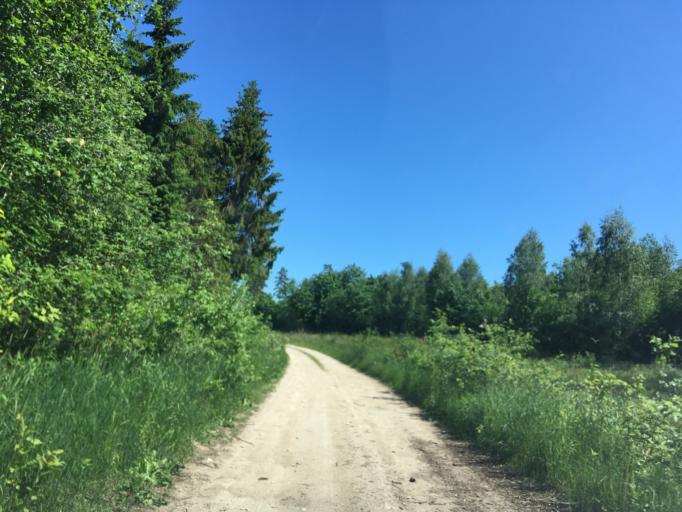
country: EE
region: Harju
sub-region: Raasiku vald
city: Raasiku
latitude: 59.1615
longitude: 25.1617
